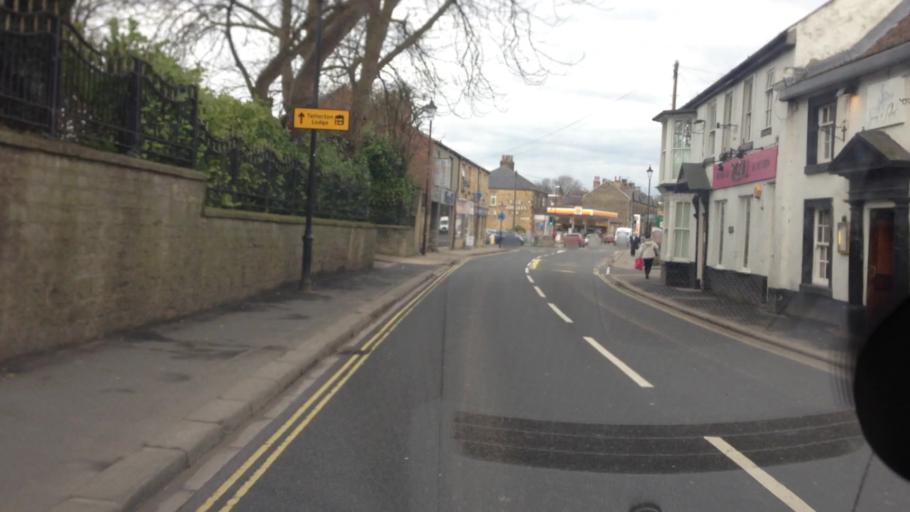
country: GB
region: England
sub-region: City and Borough of Leeds
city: Wetherby
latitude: 53.9294
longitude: -1.3853
